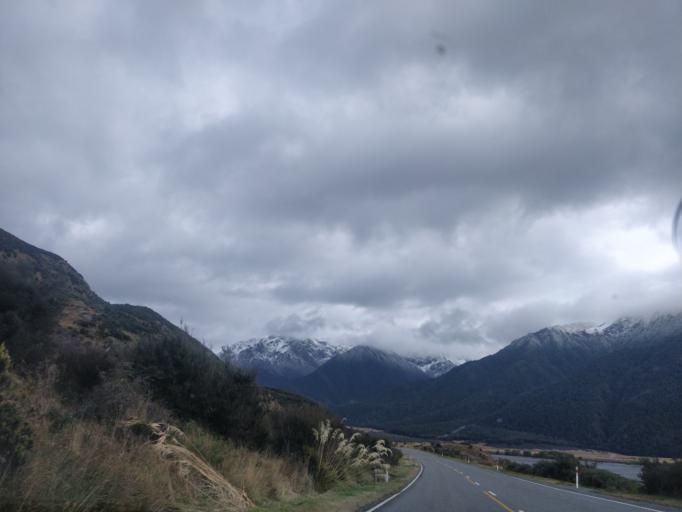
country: NZ
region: Canterbury
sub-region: Waimakariri District
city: Oxford
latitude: -43.0101
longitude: 171.7390
